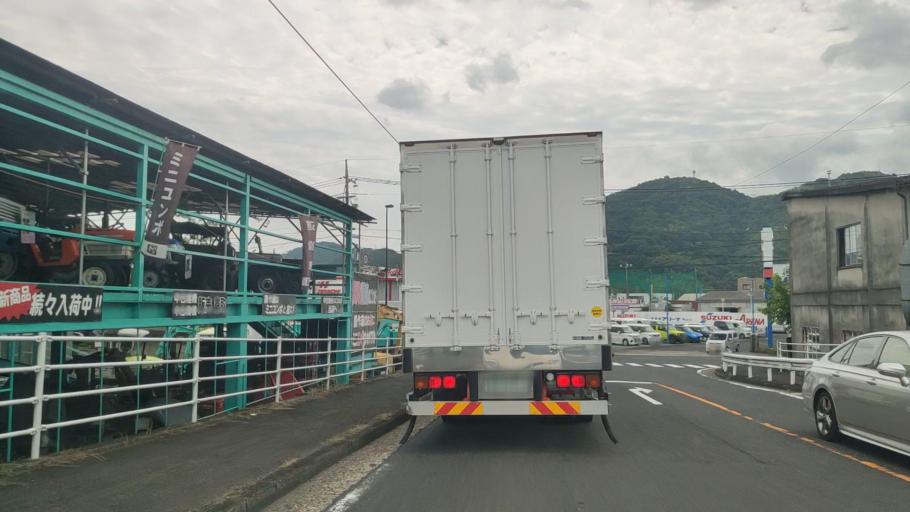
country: JP
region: Okayama
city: Tsuyama
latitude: 35.0580
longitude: 133.9812
